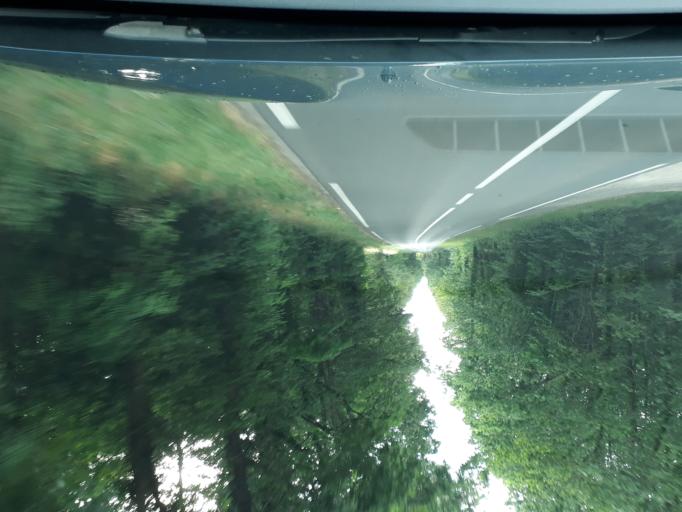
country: FR
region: Centre
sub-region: Departement du Loiret
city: Saint-Cyr-en-Val
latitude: 47.8212
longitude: 1.9681
